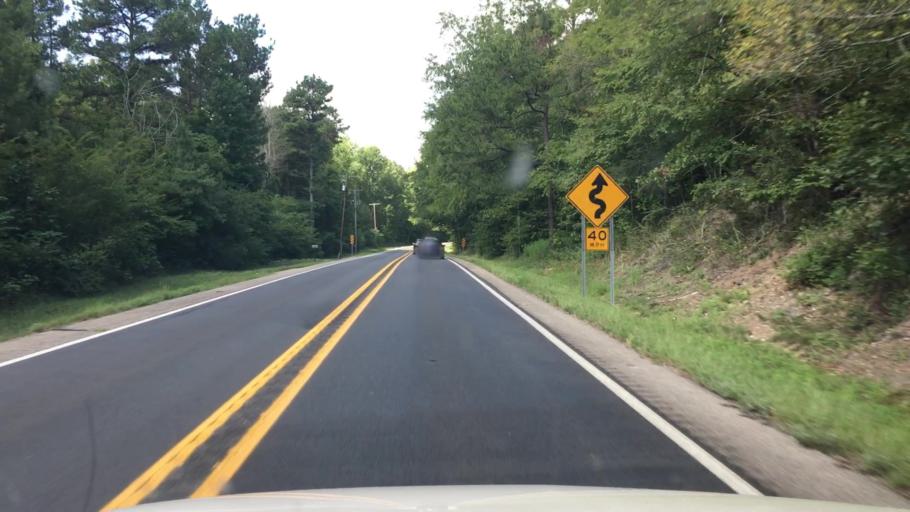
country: US
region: Arkansas
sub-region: Garland County
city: Lake Hamilton
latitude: 34.3859
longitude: -93.1247
